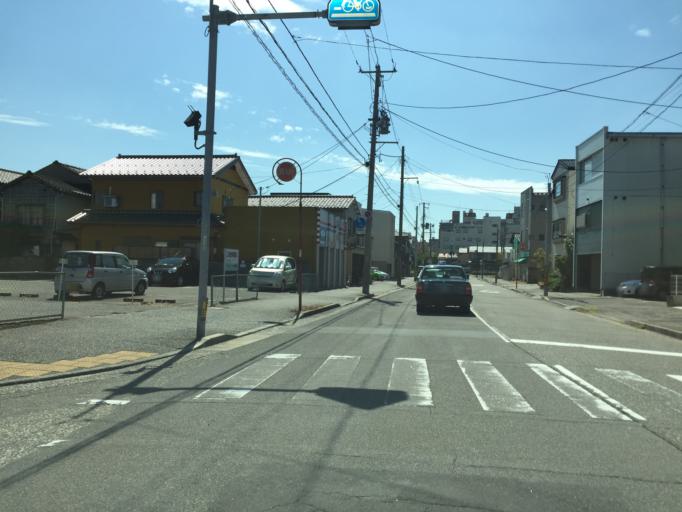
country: JP
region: Niigata
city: Niigata-shi
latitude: 37.9270
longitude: 139.0498
